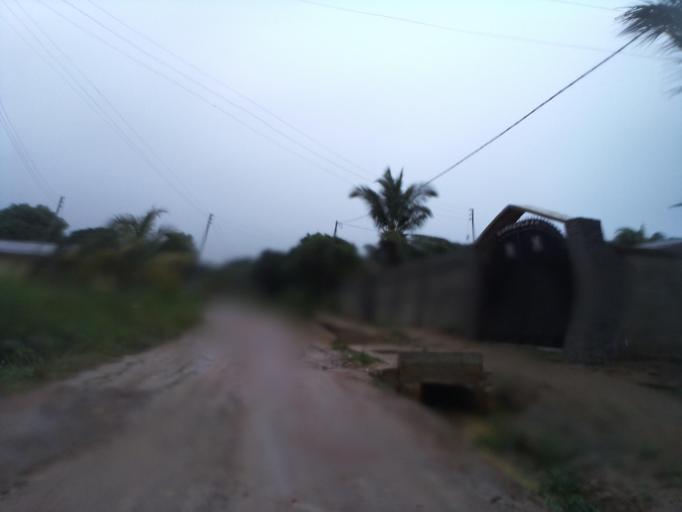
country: SL
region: Eastern Province
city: Kenema
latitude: 7.8557
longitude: -11.1915
